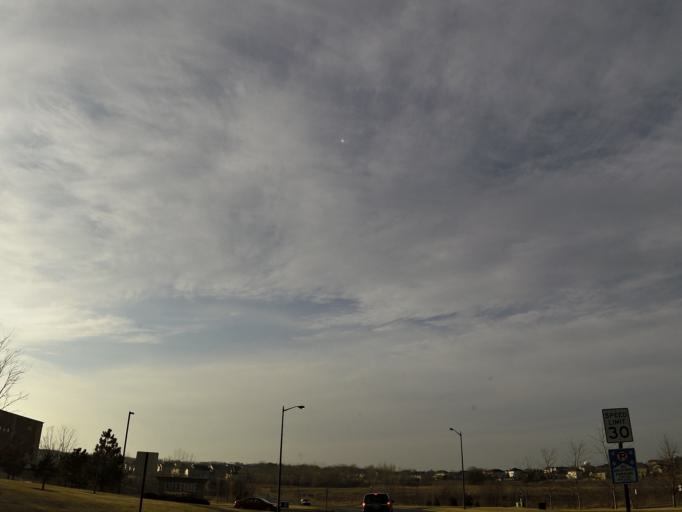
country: US
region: Minnesota
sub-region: Dakota County
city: Lakeville
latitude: 44.6845
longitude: -93.2486
